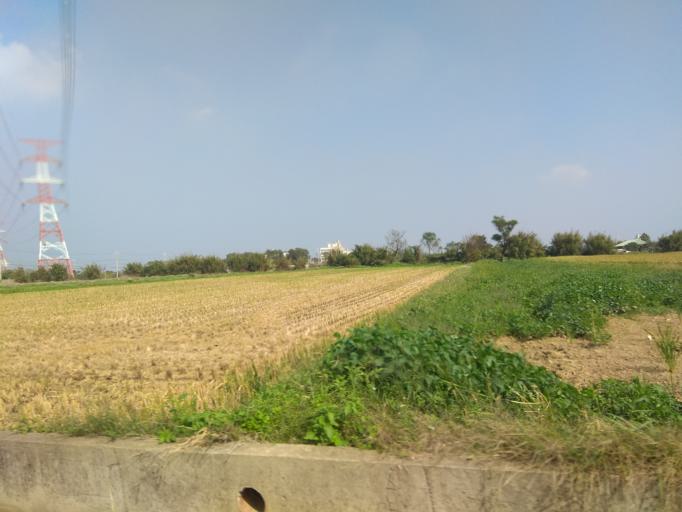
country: TW
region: Taiwan
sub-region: Hsinchu
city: Zhubei
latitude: 24.9978
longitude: 121.0604
